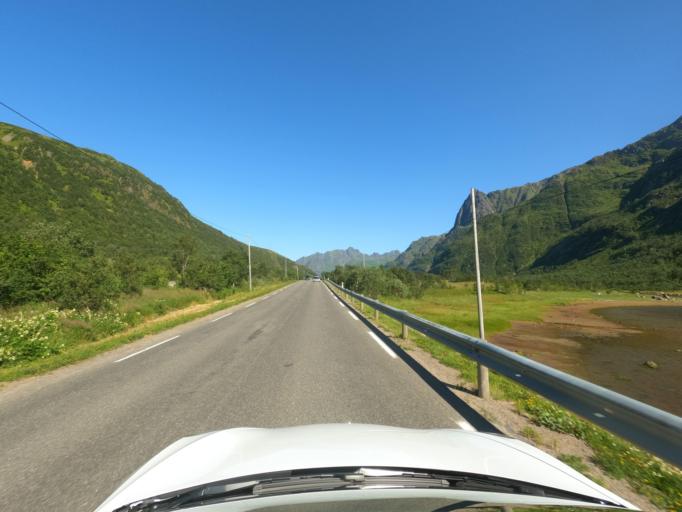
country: NO
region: Nordland
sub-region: Hadsel
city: Melbu
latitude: 68.3686
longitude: 14.7692
